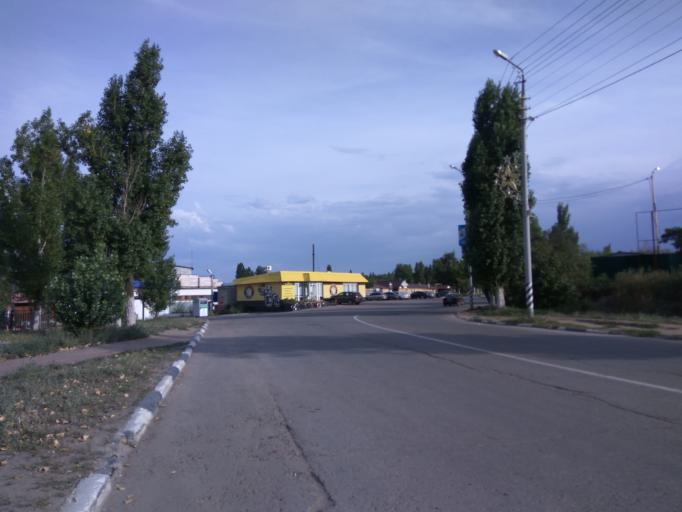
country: RU
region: Saratov
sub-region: Saratovskiy Rayon
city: Saratov
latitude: 51.5496
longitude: 46.0533
